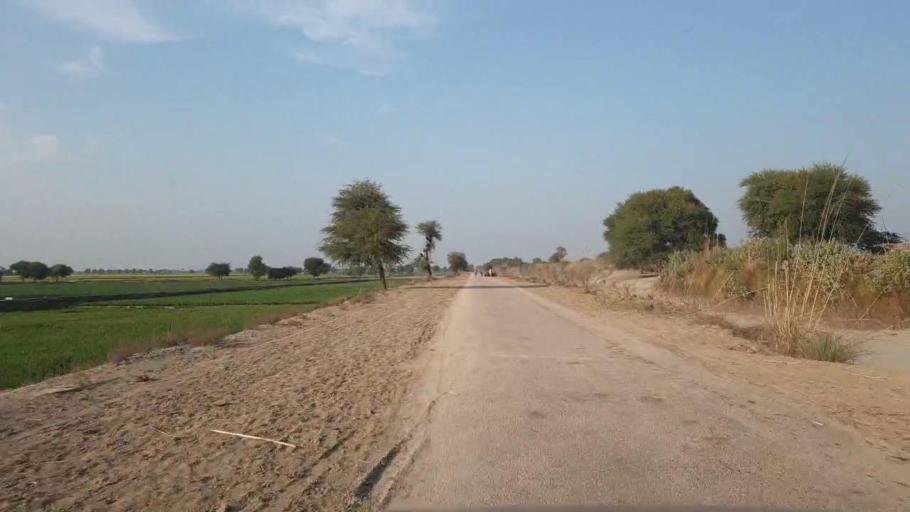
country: PK
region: Sindh
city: Shahpur Chakar
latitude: 26.1633
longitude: 68.6406
